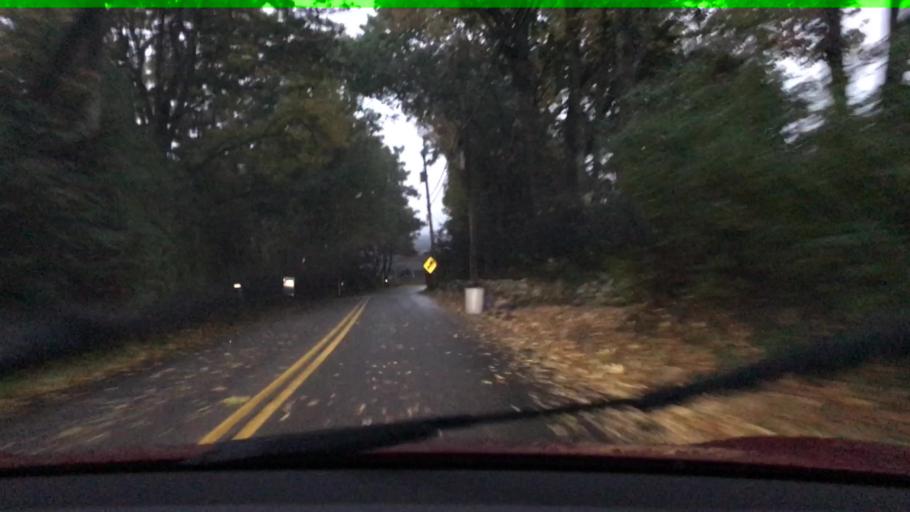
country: US
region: Maine
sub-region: York County
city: Cape Neddick
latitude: 43.2105
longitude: -70.5879
